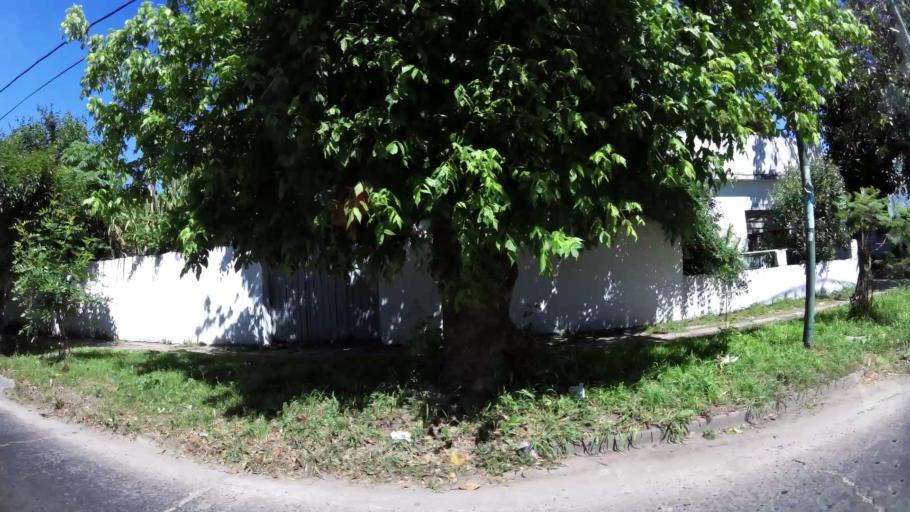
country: AR
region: Buenos Aires
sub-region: Partido de General San Martin
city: General San Martin
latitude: -34.5313
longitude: -58.5572
